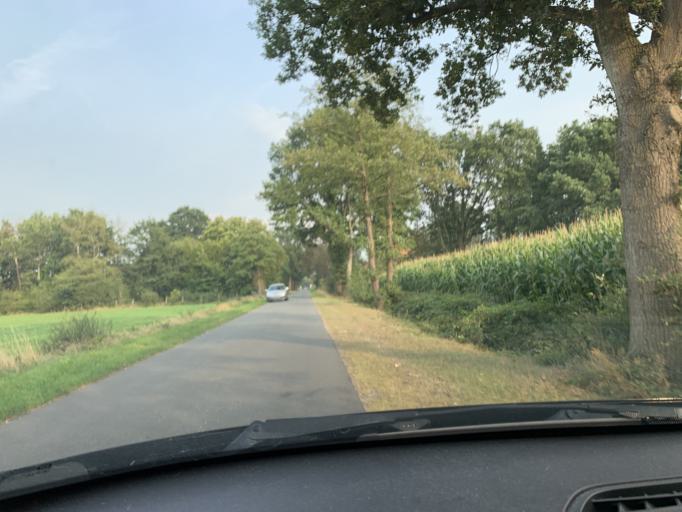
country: DE
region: Lower Saxony
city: Westerstede
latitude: 53.2582
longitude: 7.8871
